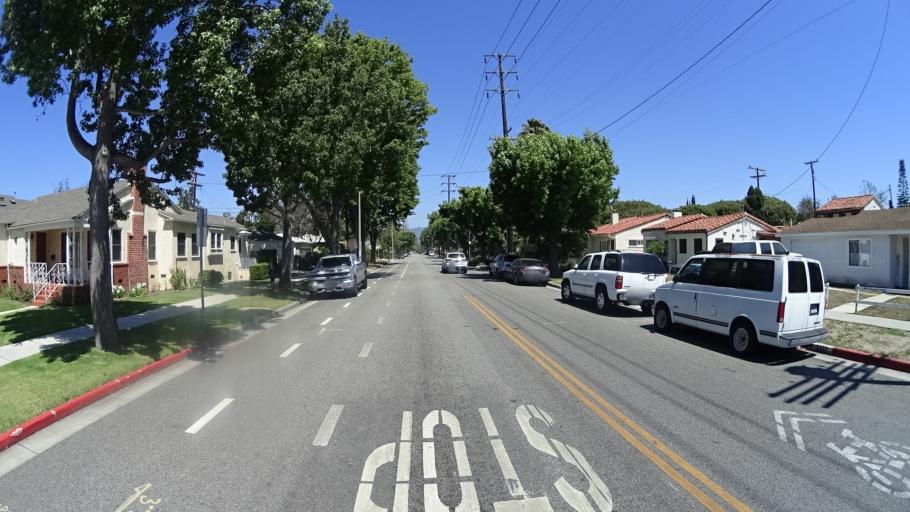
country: US
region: California
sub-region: Los Angeles County
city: Santa Monica
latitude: 34.0134
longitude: -118.4732
